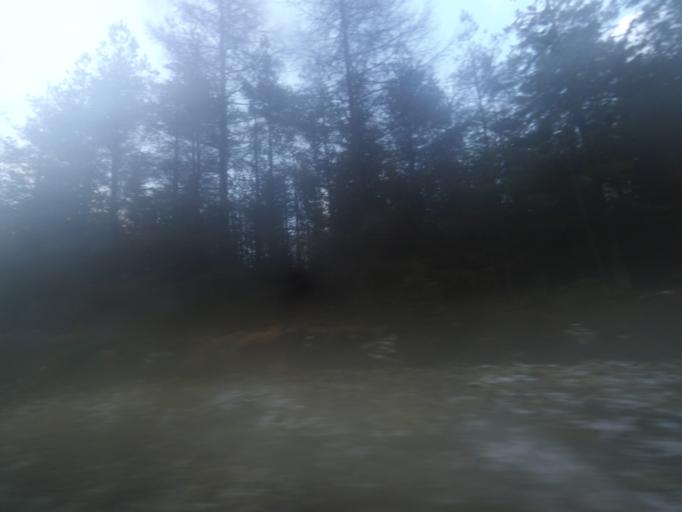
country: DK
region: Central Jutland
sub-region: Ikast-Brande Kommune
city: Brande
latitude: 56.0160
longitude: 9.1621
